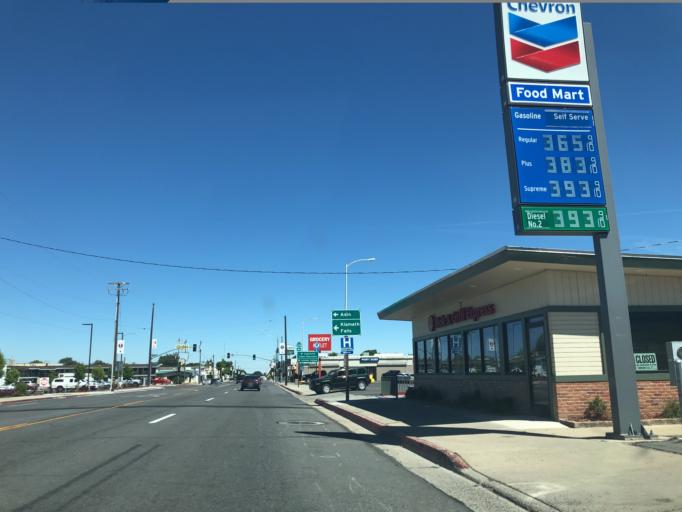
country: US
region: California
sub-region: Lassen County
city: Susanville
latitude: 40.4158
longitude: -120.6504
